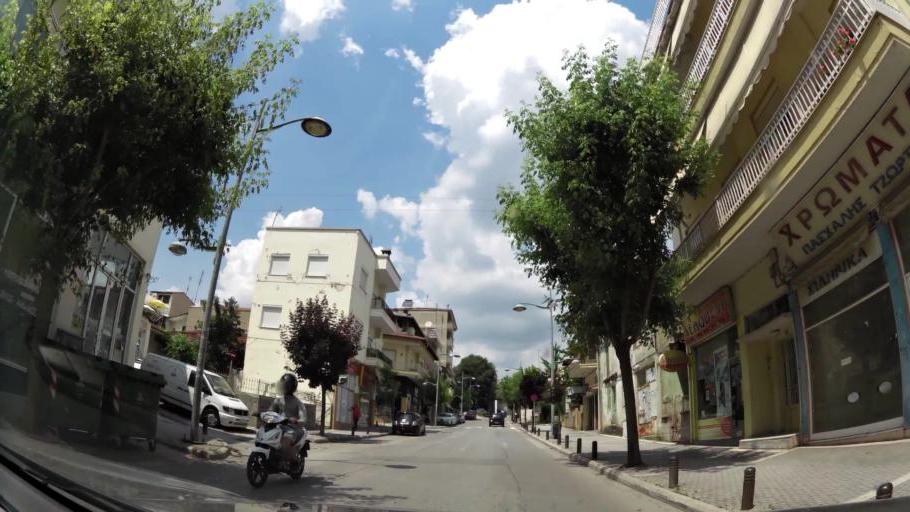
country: GR
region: West Macedonia
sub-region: Nomos Kozanis
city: Kozani
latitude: 40.3046
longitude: 21.7890
